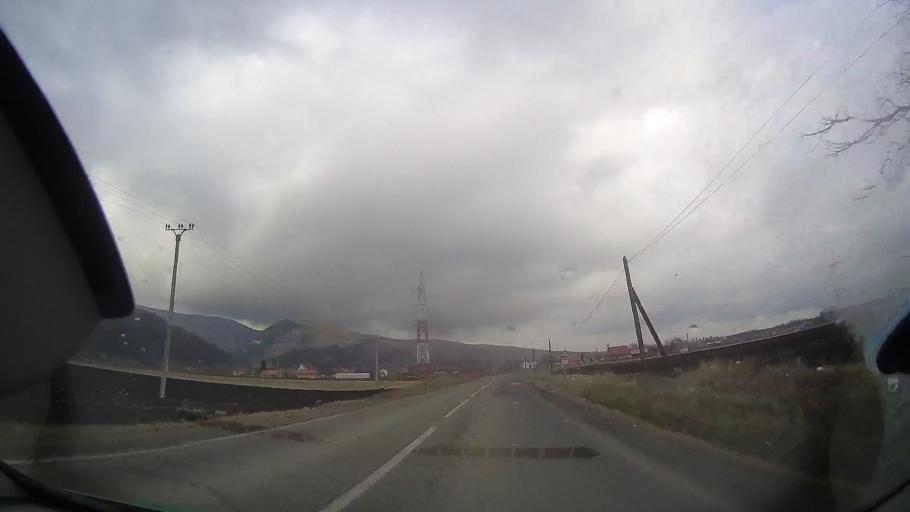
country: RO
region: Cluj
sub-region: Comuna Moldovenesti
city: Moldovenesti
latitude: 46.5166
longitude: 23.6805
